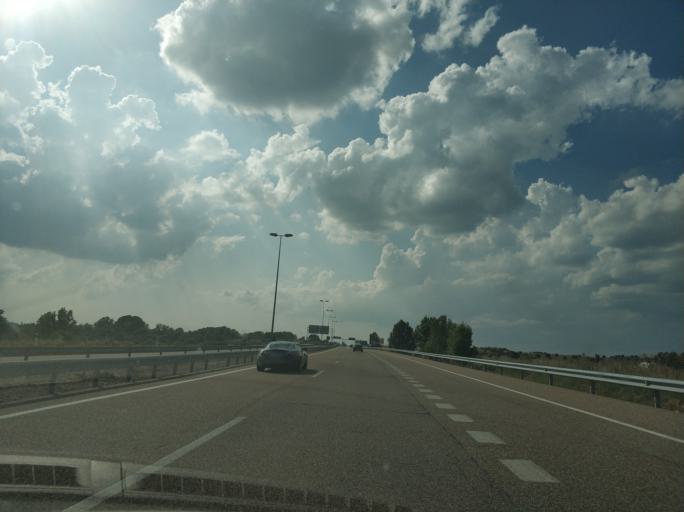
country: ES
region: Castille and Leon
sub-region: Provincia de Leon
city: Valverde de la Virgen
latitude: 42.5791
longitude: -5.6683
